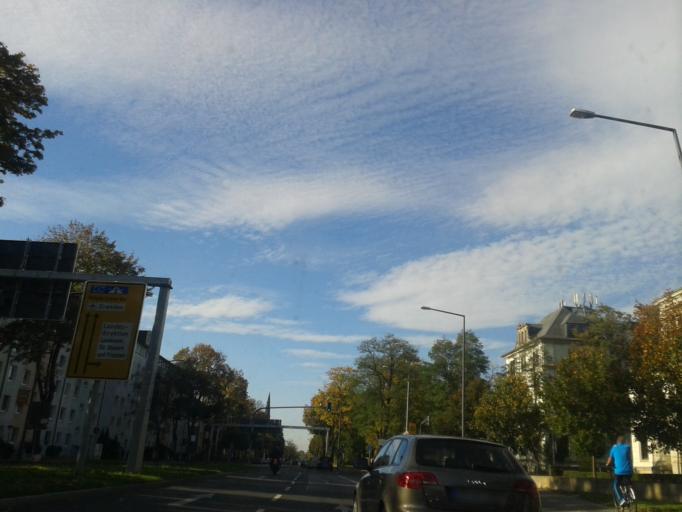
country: DE
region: Saxony
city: Albertstadt
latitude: 51.0713
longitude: 13.7715
